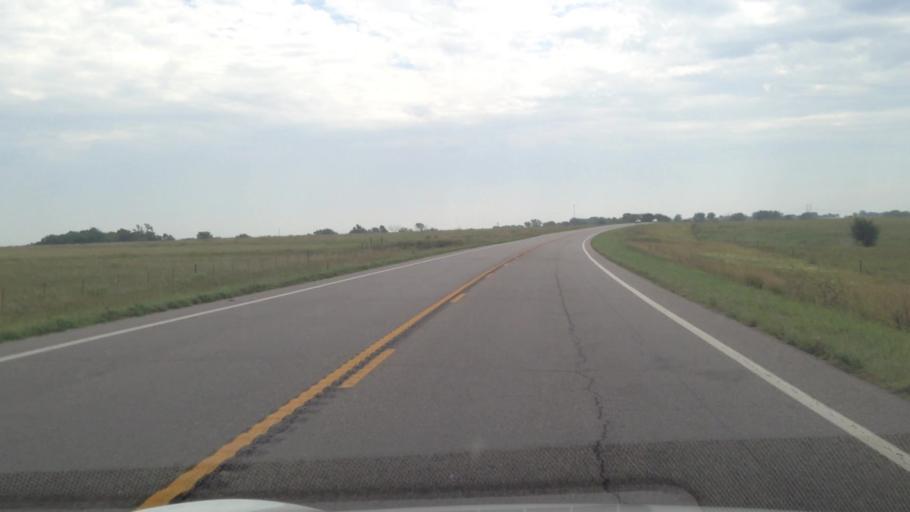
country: US
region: Kansas
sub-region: Bourbon County
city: Fort Scott
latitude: 37.8810
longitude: -95.0098
